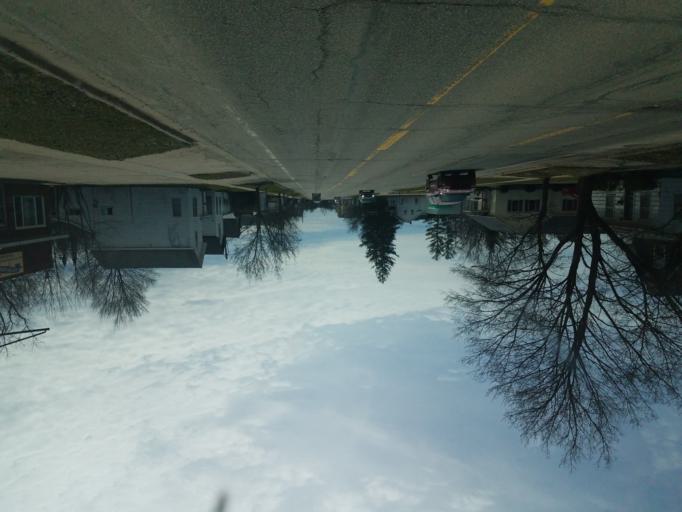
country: US
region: Michigan
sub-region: Osceola County
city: Reed City
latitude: 43.8790
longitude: -85.5100
